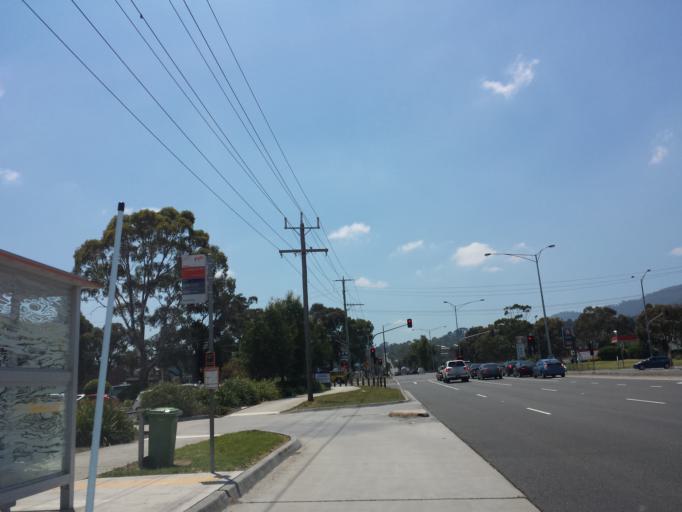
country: AU
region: Victoria
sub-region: Maroondah
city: Kilsyth South
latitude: -37.8183
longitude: 145.3159
